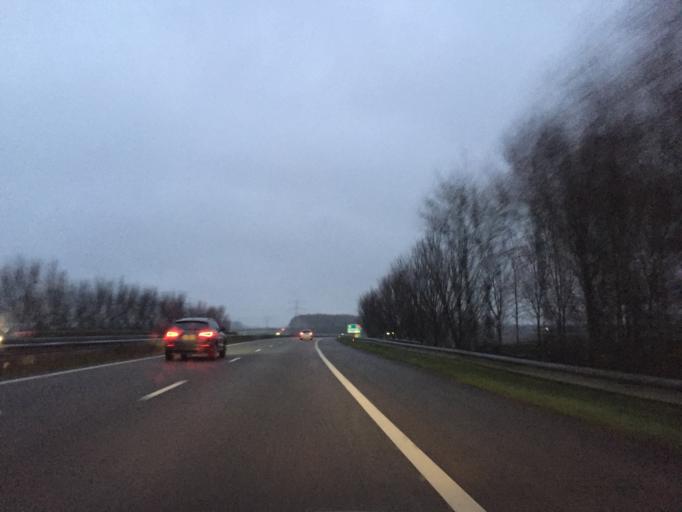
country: NL
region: North Brabant
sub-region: Gemeente Moerdijk
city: Klundert
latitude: 51.6163
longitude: 4.5062
